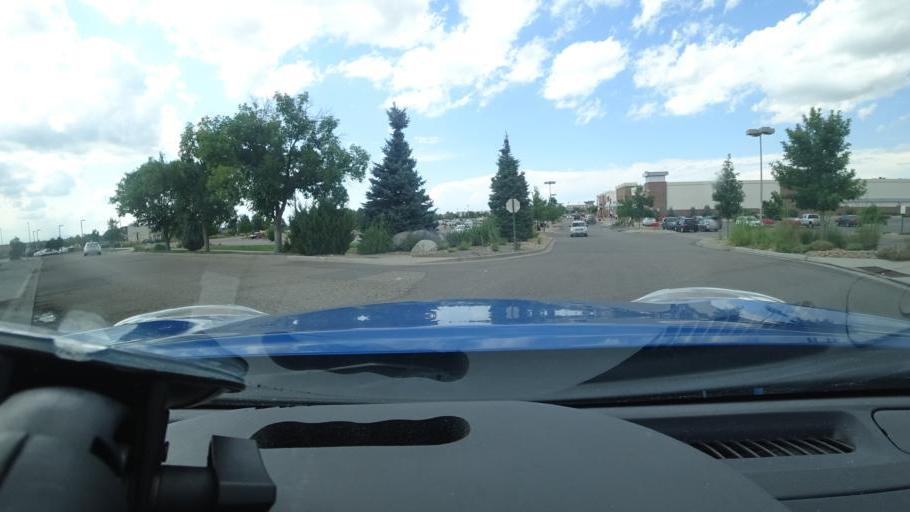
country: US
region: Colorado
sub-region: Adams County
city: Aurora
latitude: 39.6900
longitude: -104.8638
